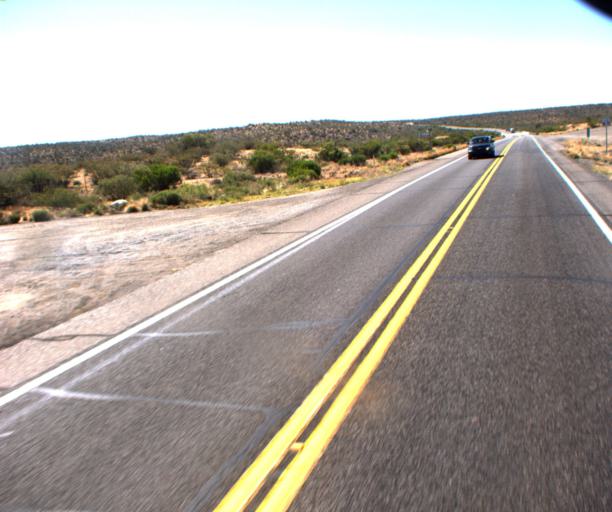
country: US
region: Arizona
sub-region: Yavapai County
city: Congress
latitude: 34.2091
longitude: -113.0652
